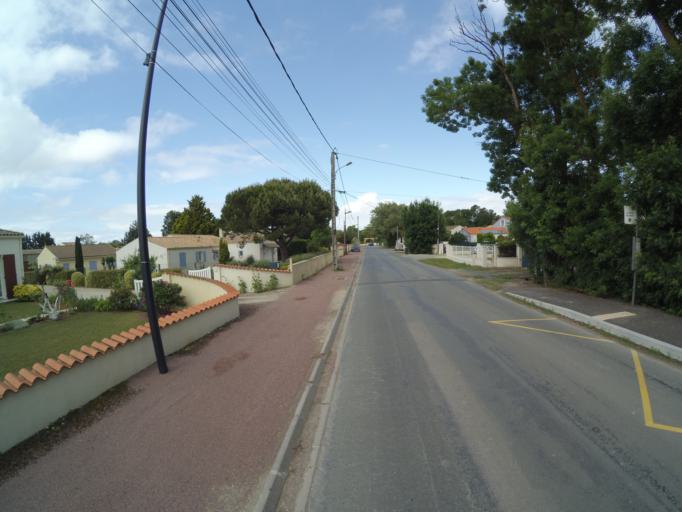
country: FR
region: Poitou-Charentes
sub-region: Departement de la Charente-Maritime
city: Chatelaillon-Plage
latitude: 46.0585
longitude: -1.0716
